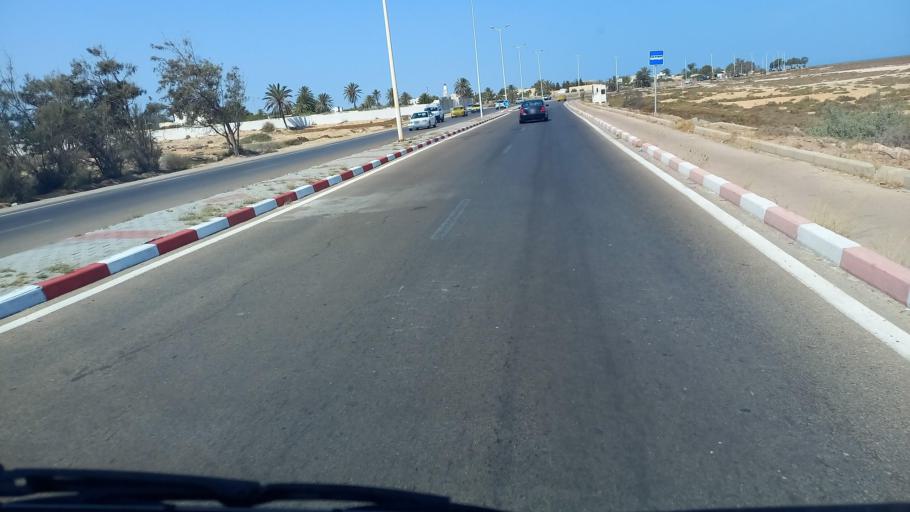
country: TN
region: Madanin
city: Midoun
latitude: 33.8695
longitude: 10.9399
